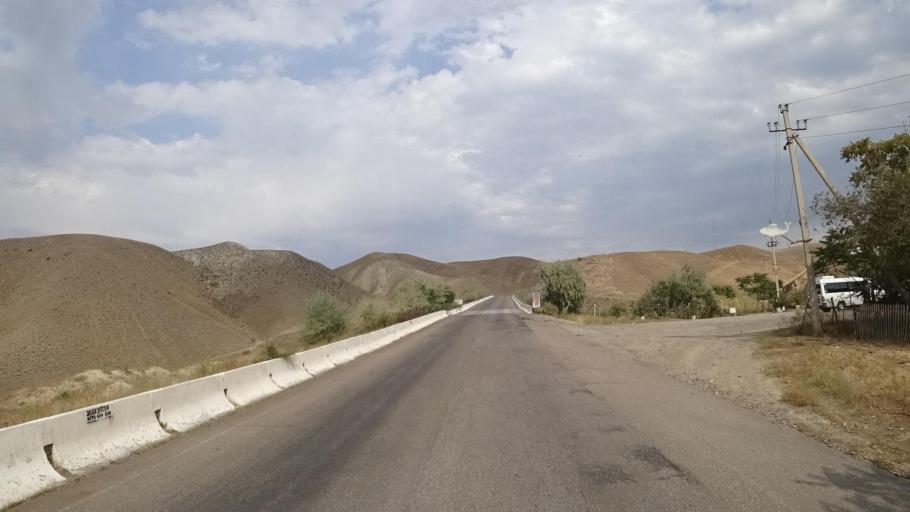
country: KG
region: Jalal-Abad
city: Toktogul
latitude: 41.7804
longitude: 72.9883
